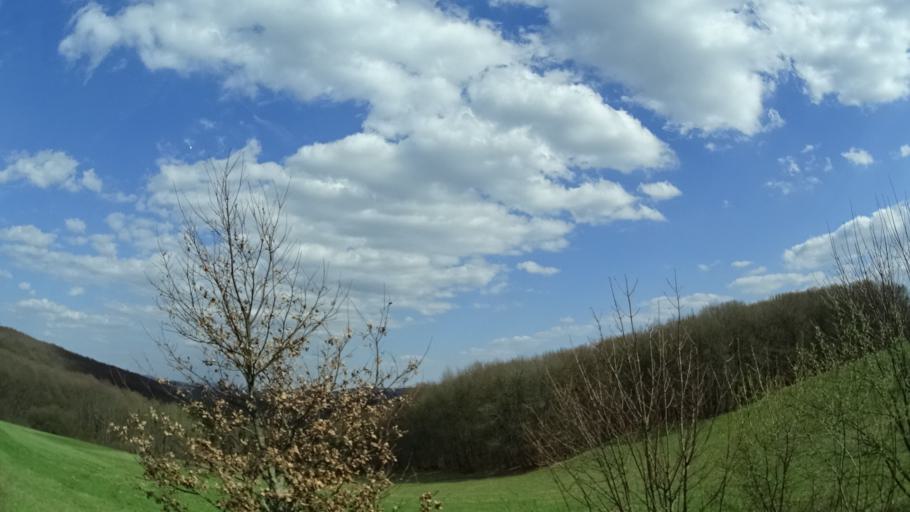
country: DE
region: Rheinland-Pfalz
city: Herborn
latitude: 49.7674
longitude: 7.2996
